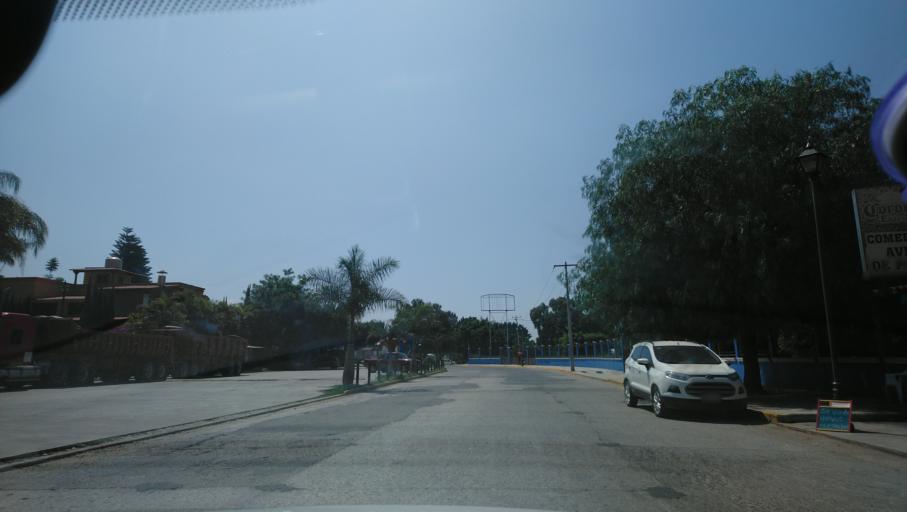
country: MX
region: Oaxaca
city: Santa Maria del Tule
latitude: 17.0446
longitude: -96.6344
